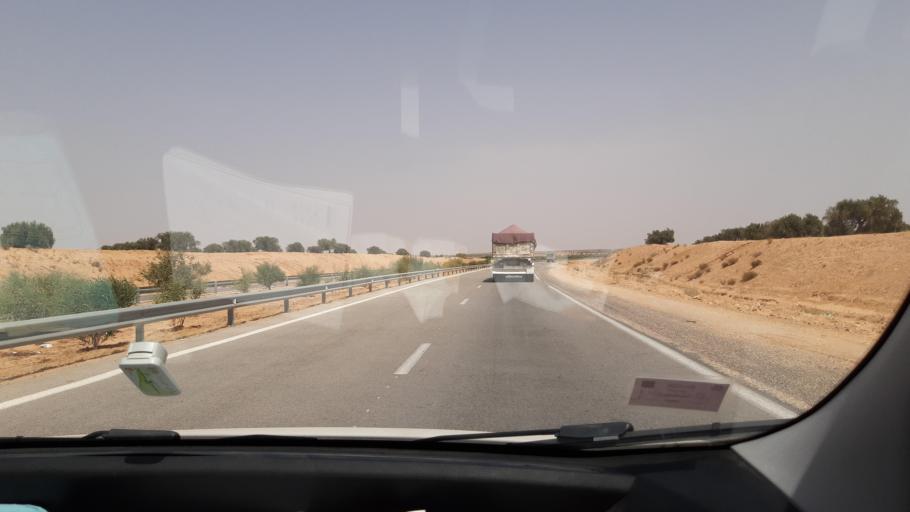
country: TN
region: Safaqis
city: Bi'r `Ali Bin Khalifah
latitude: 34.5285
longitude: 10.0871
